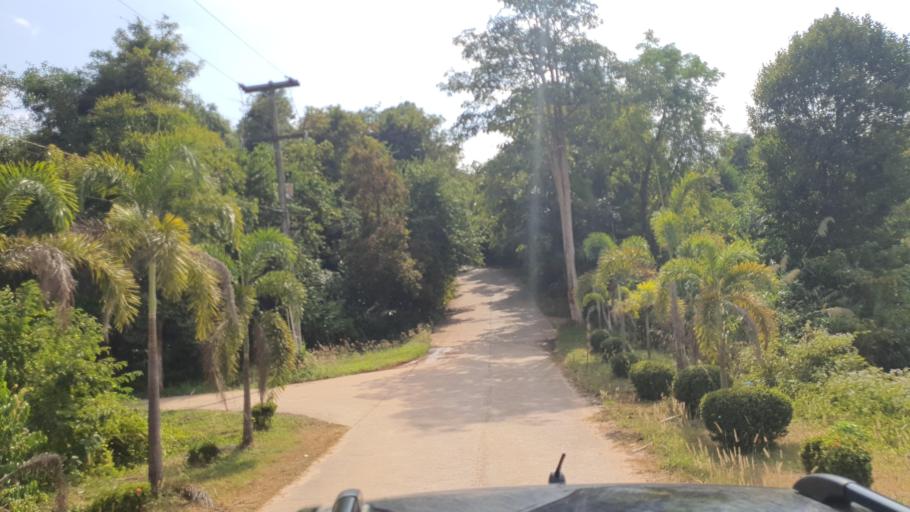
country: TH
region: Changwat Bueng Kan
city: Si Wilai
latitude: 18.2743
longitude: 103.7962
